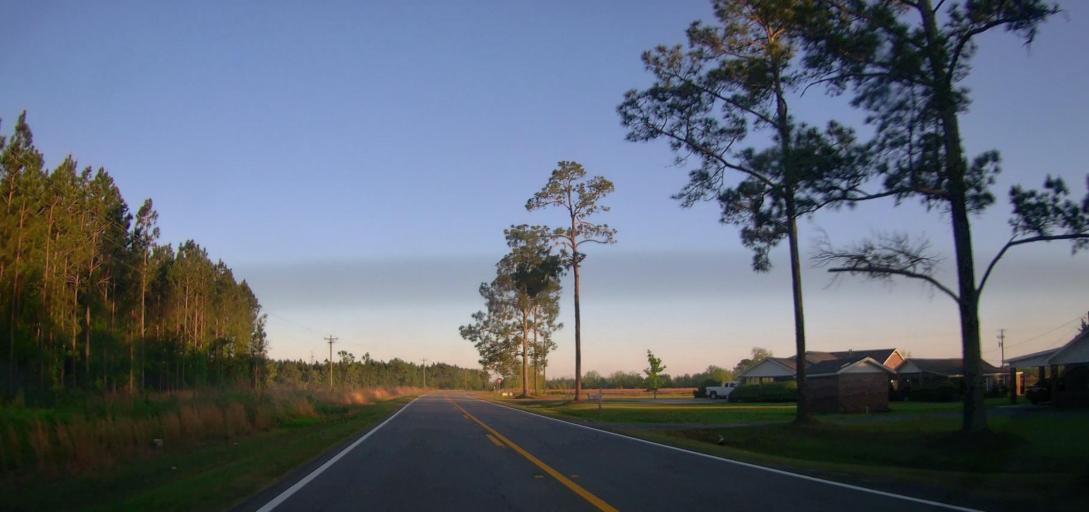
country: US
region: Georgia
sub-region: Irwin County
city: Ocilla
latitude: 31.6170
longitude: -83.2666
